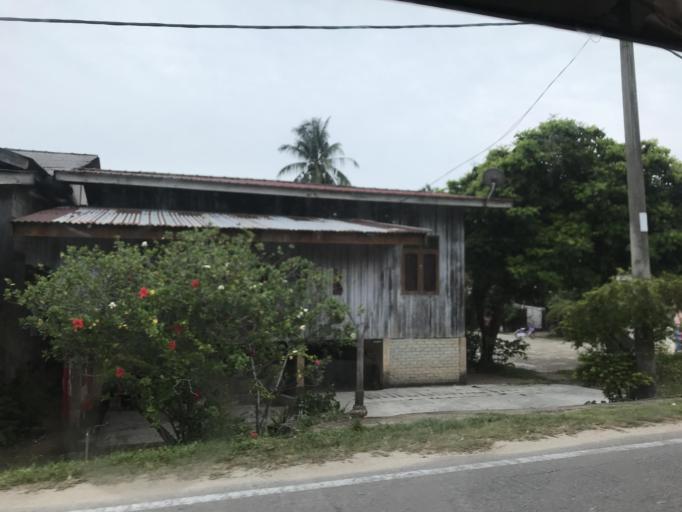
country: MY
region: Kelantan
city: Kota Bharu
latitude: 6.1766
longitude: 102.2228
